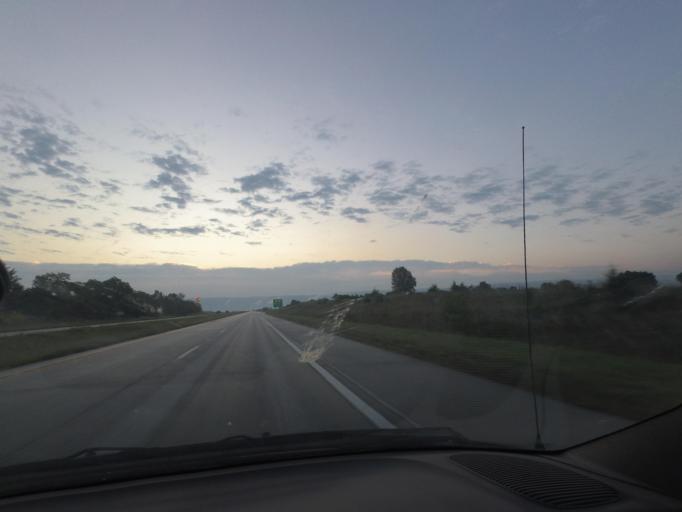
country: US
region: Missouri
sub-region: Macon County
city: Macon
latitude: 39.7605
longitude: -92.5720
